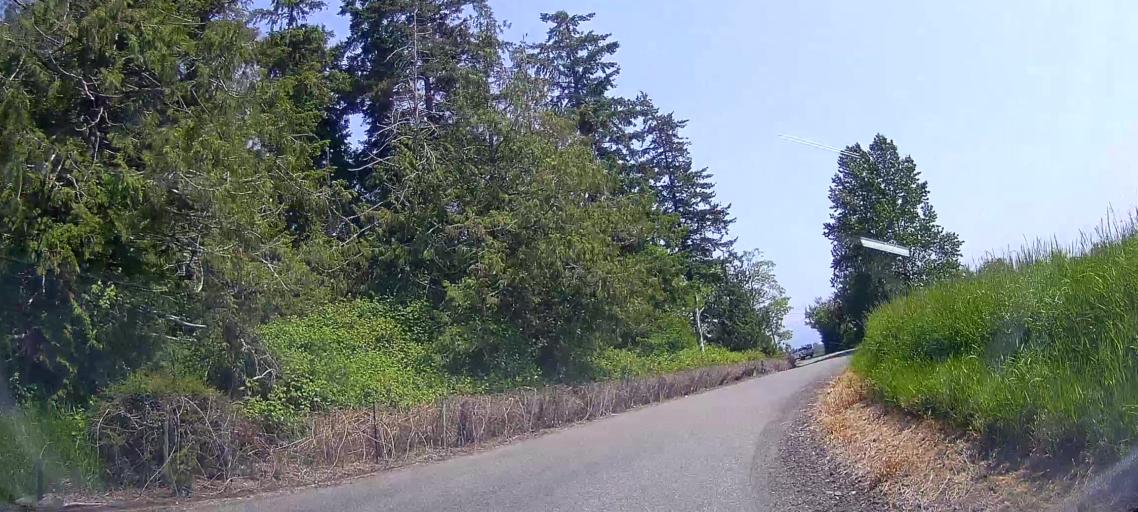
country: US
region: Washington
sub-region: Skagit County
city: Mount Vernon
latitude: 48.4585
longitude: -122.4118
